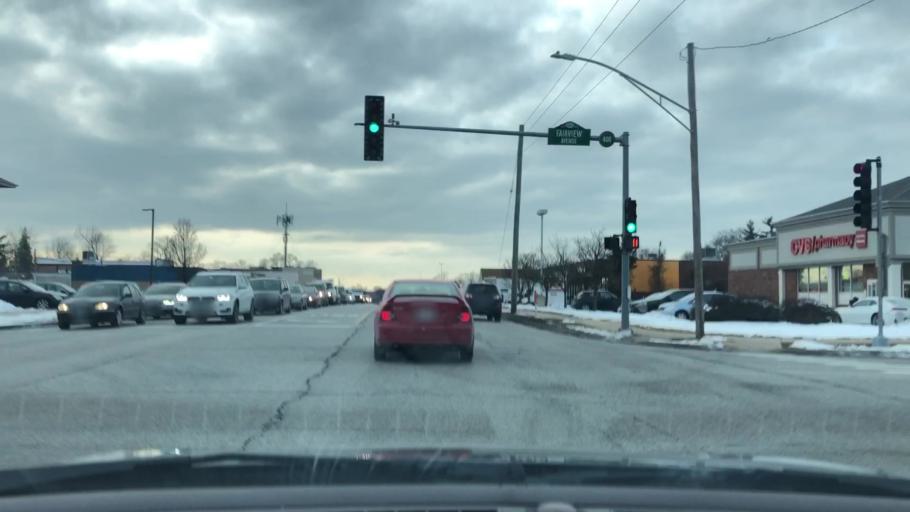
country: US
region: Illinois
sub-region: DuPage County
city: Downers Grove
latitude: 41.8096
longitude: -87.9953
